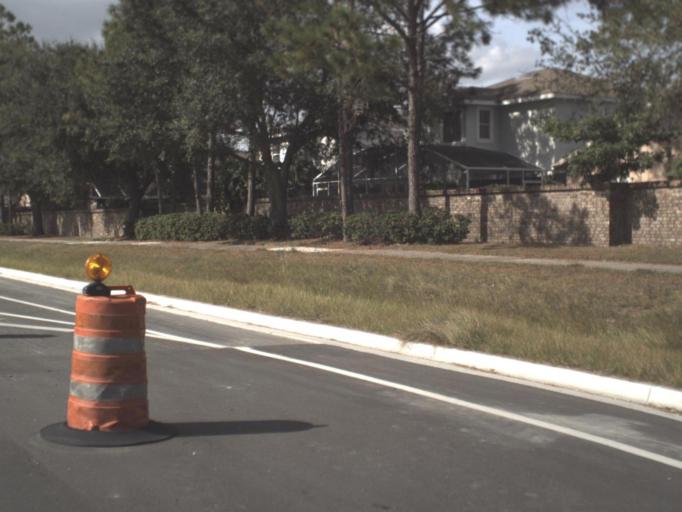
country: US
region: Florida
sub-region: Osceola County
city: Buenaventura Lakes
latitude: 28.3450
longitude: -81.3318
